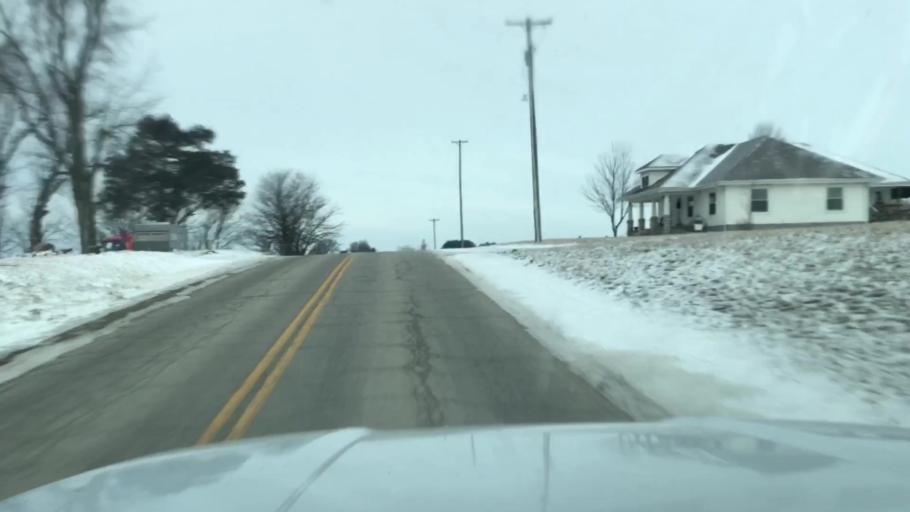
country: US
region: Missouri
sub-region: Andrew County
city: Savannah
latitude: 40.0247
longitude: -94.9238
